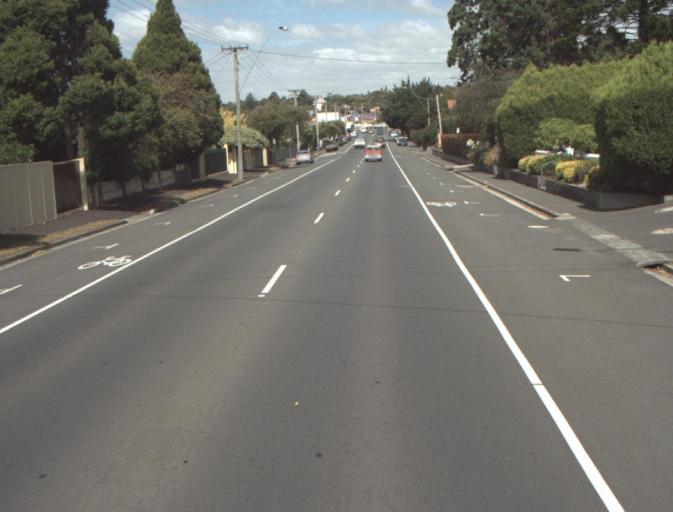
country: AU
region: Tasmania
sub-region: Launceston
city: East Launceston
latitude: -41.4390
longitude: 147.1589
